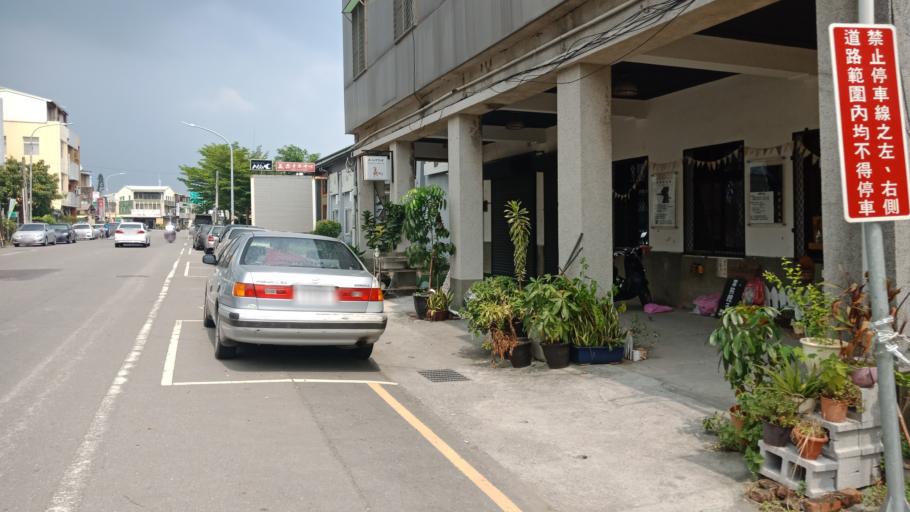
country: TW
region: Taiwan
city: Xinying
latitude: 23.3080
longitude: 120.3235
